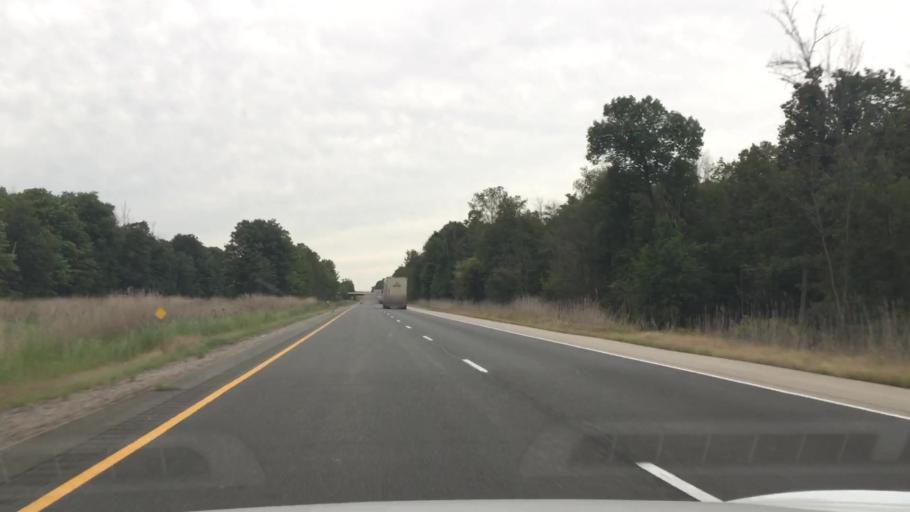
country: CA
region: Ontario
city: Lambton Shores
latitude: 42.9923
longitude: -81.7794
